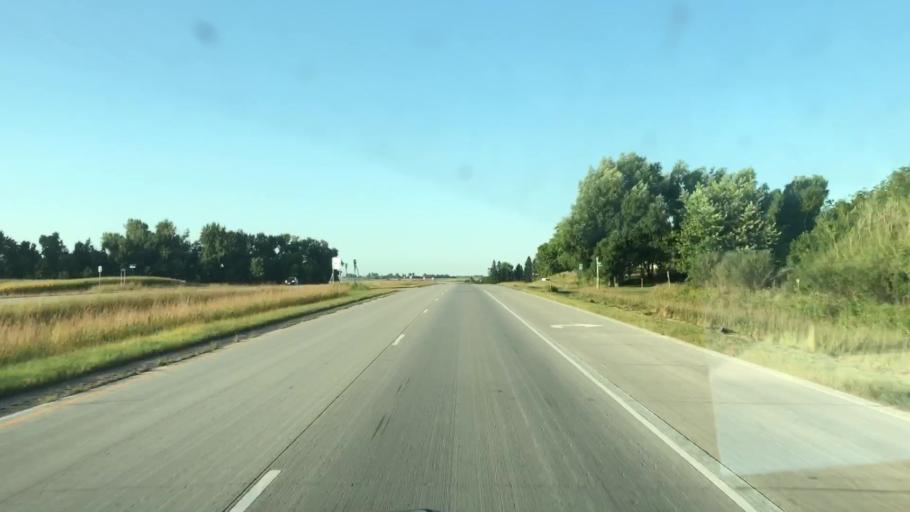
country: US
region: Minnesota
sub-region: Nobles County
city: Worthington
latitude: 43.5815
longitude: -95.6499
